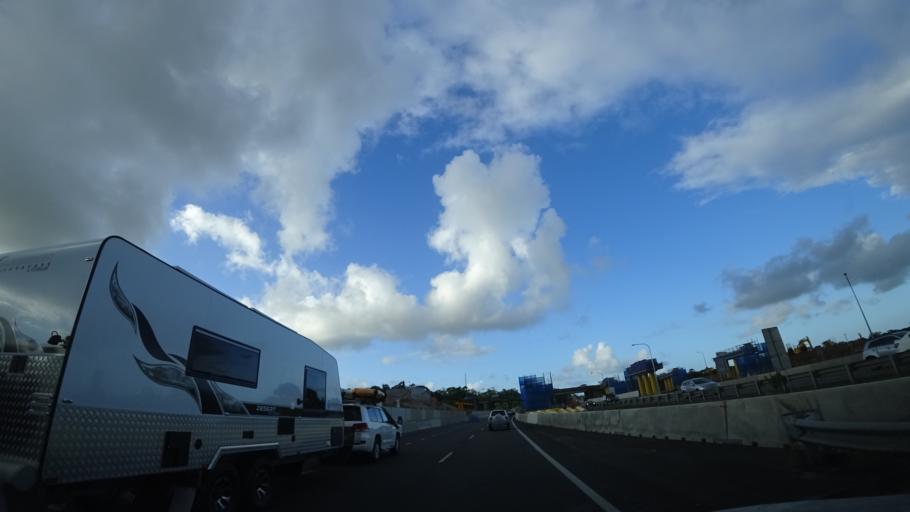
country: AU
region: Queensland
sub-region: Sunshine Coast
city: Little Mountain
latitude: -26.7748
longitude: 153.0428
